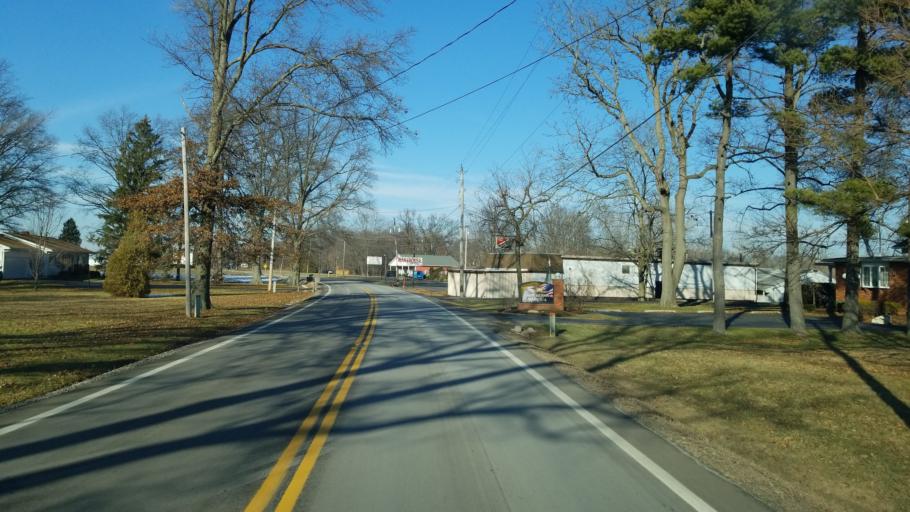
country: US
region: Ohio
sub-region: Huron County
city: Norwalk
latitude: 41.2167
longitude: -82.6386
